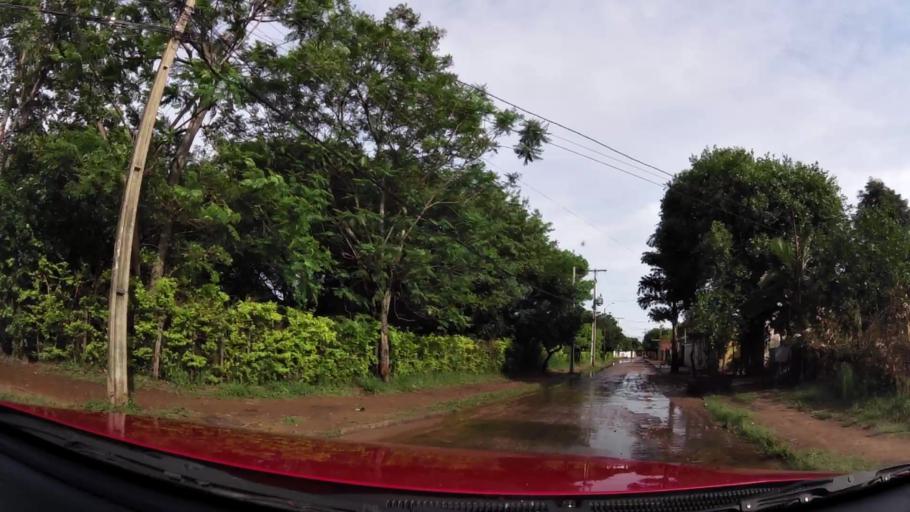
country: PY
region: Central
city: Limpio
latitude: -25.1701
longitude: -57.4832
